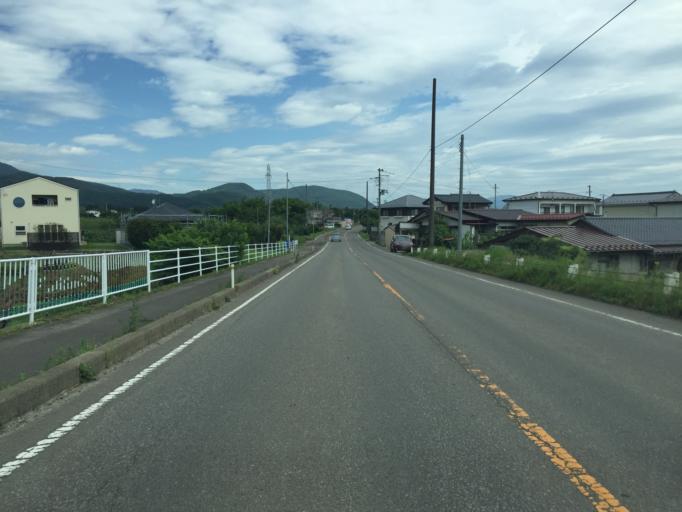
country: JP
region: Fukushima
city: Fukushima-shi
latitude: 37.7731
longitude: 140.3861
